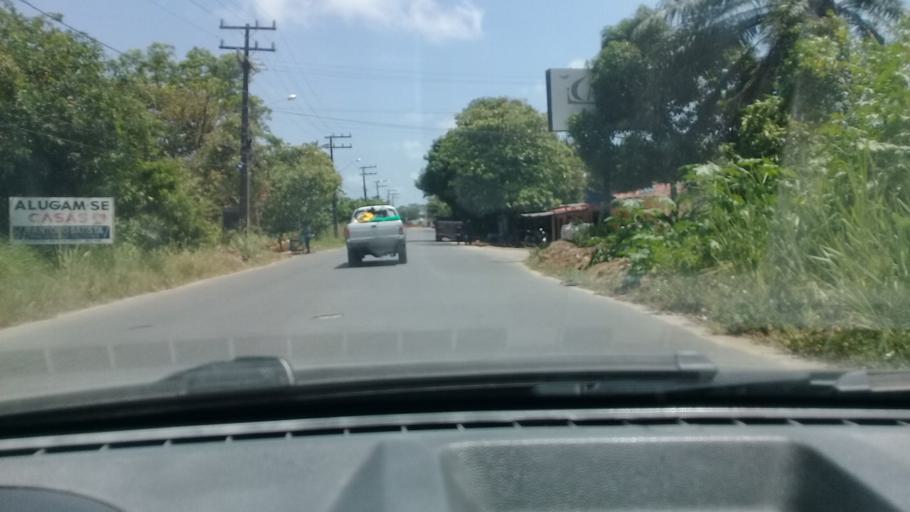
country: BR
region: Pernambuco
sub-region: Itamaraca
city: Itamaraca
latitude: -7.7736
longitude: -34.8367
